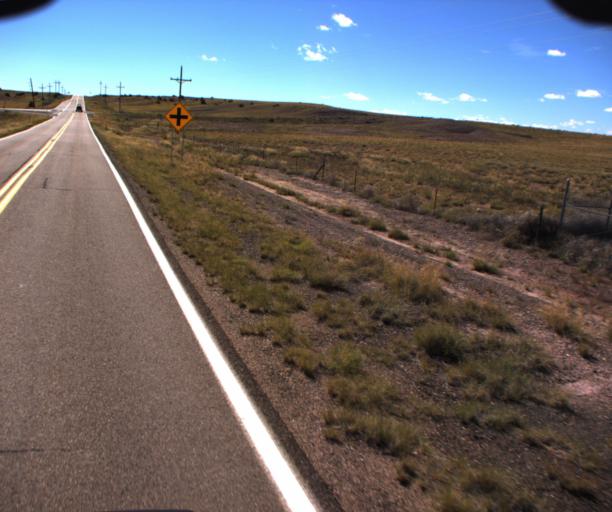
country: US
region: Arizona
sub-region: Apache County
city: Saint Johns
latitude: 34.5724
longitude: -109.3368
